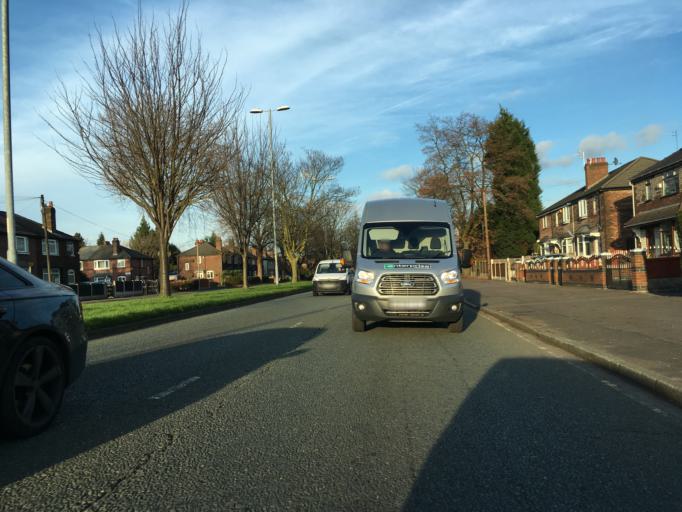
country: GB
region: England
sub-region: Manchester
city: Burnage
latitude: 53.4219
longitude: -2.2128
